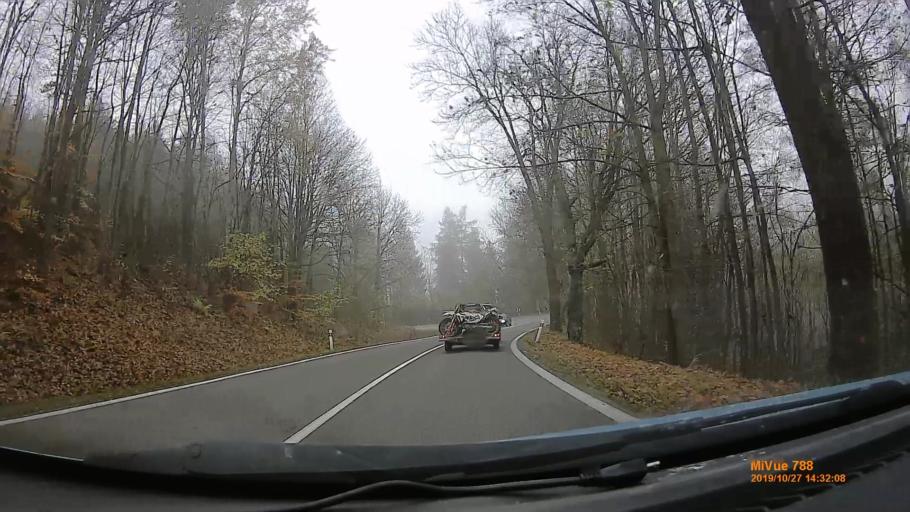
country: CZ
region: Olomoucky
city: Olsany
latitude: 49.9859
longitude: 16.8147
